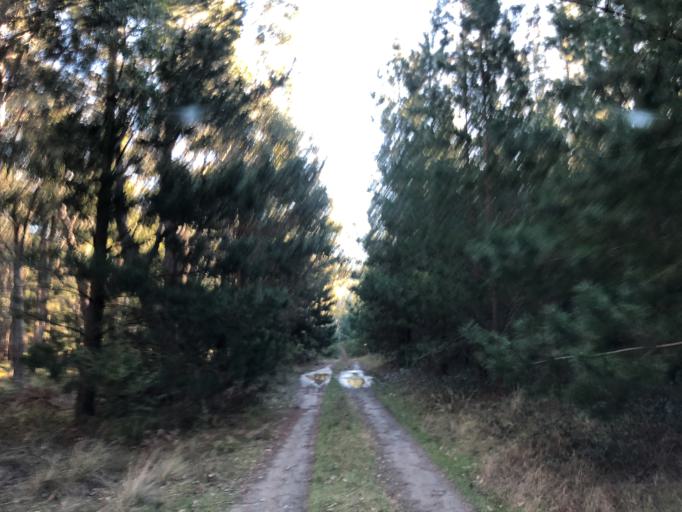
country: AU
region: Victoria
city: Brown Hill
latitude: -37.5068
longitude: 144.1553
